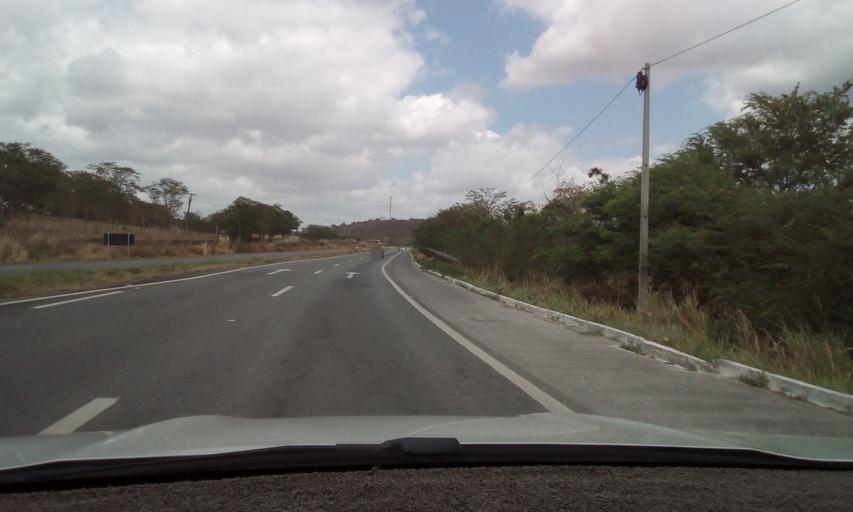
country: BR
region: Paraiba
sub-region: Fagundes
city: Fagundes
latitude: -7.2774
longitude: -35.7371
